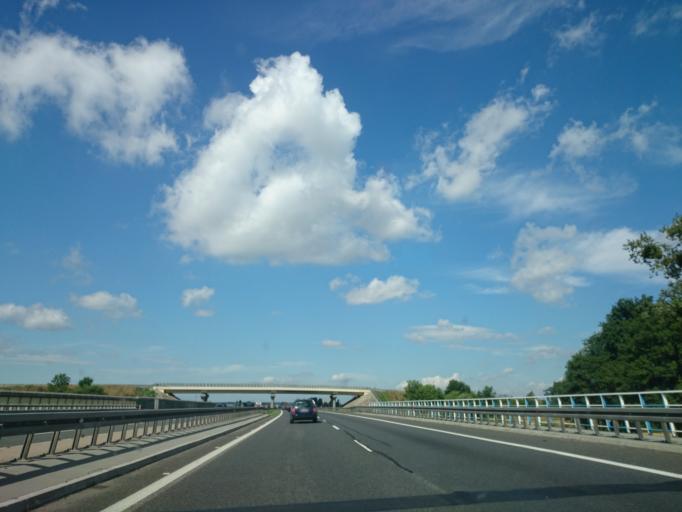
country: PL
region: Opole Voivodeship
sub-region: Powiat brzeski
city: Lewin Brzeski
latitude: 50.7092
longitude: 17.6033
